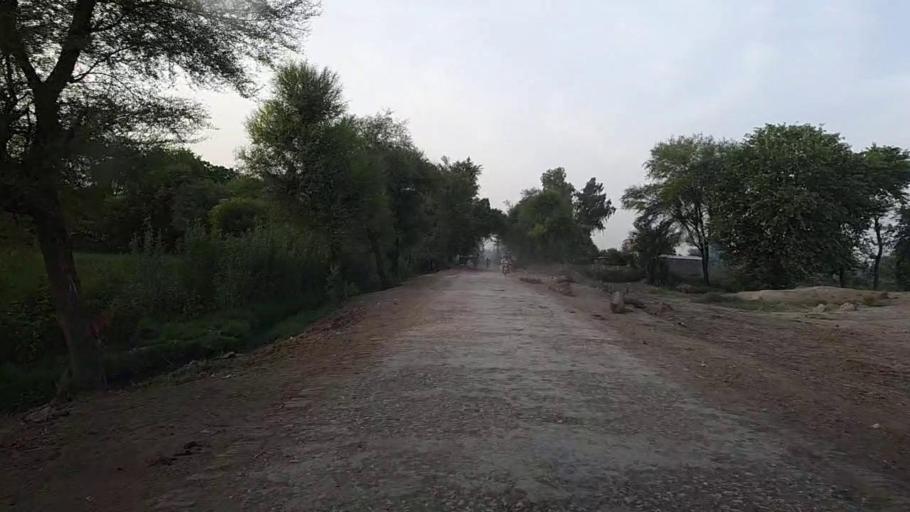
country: PK
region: Sindh
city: Ubauro
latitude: 28.2922
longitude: 69.7996
